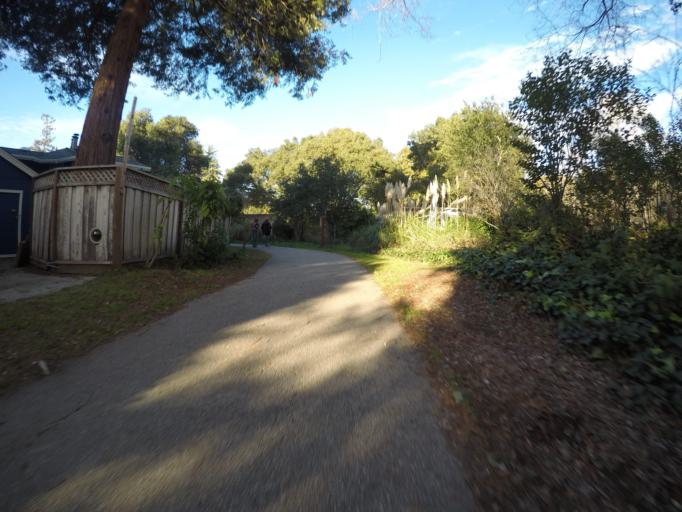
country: US
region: California
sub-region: Santa Cruz County
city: Santa Cruz
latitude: 36.9848
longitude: -122.0153
